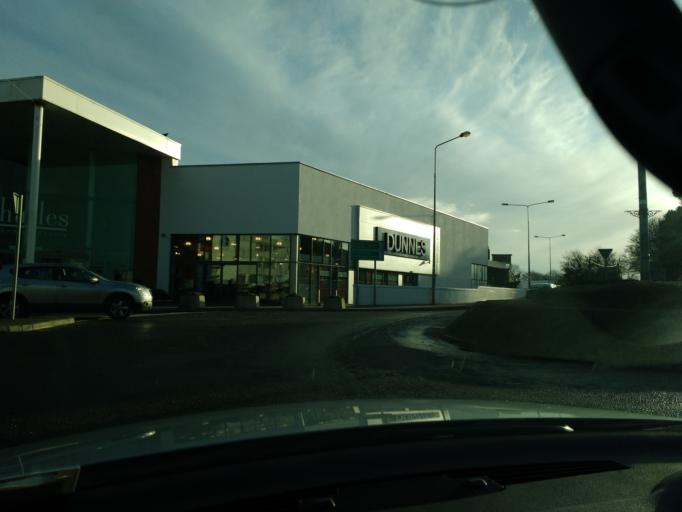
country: IE
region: Munster
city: Thurles
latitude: 52.6753
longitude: -7.8118
